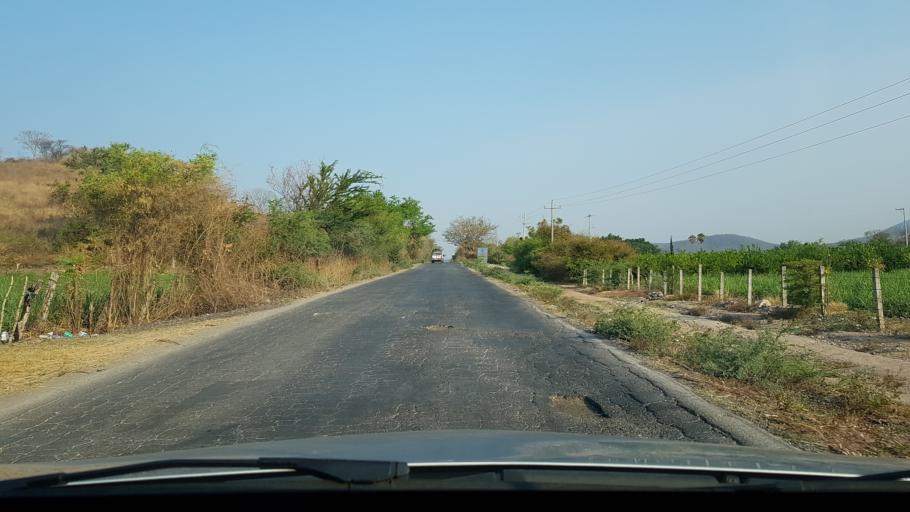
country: MX
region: Morelos
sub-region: Tepalcingo
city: Zacapalco
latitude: 18.6424
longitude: -99.0196
